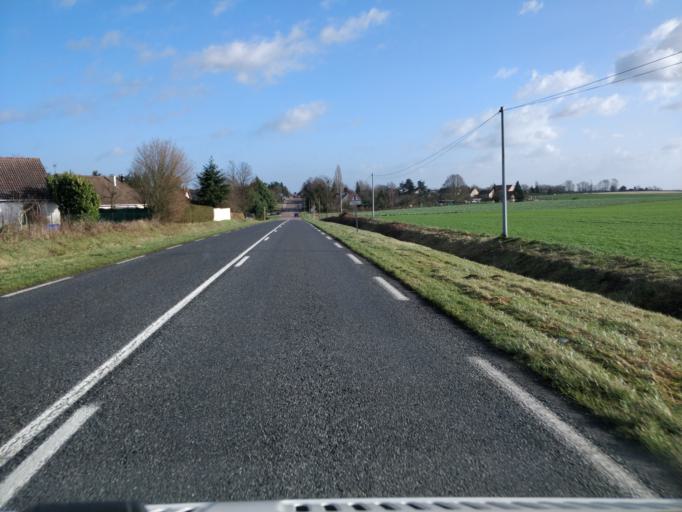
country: FR
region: Bourgogne
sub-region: Departement de l'Yonne
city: Cheroy
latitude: 48.2014
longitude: 2.9843
